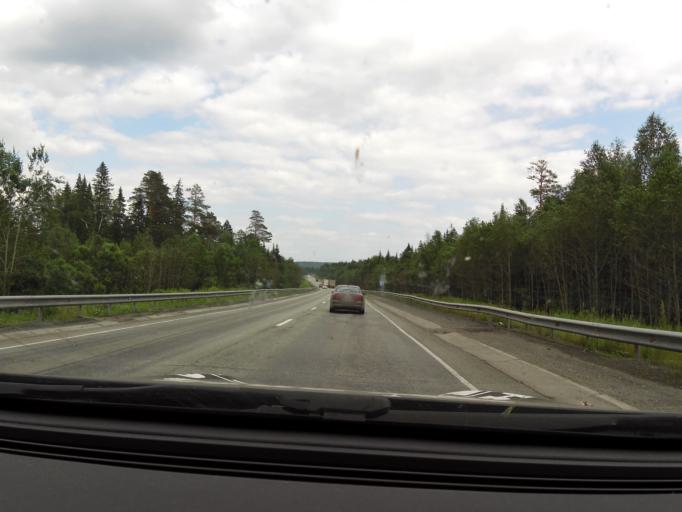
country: RU
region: Sverdlovsk
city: Bilimbay
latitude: 56.8530
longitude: 59.7797
